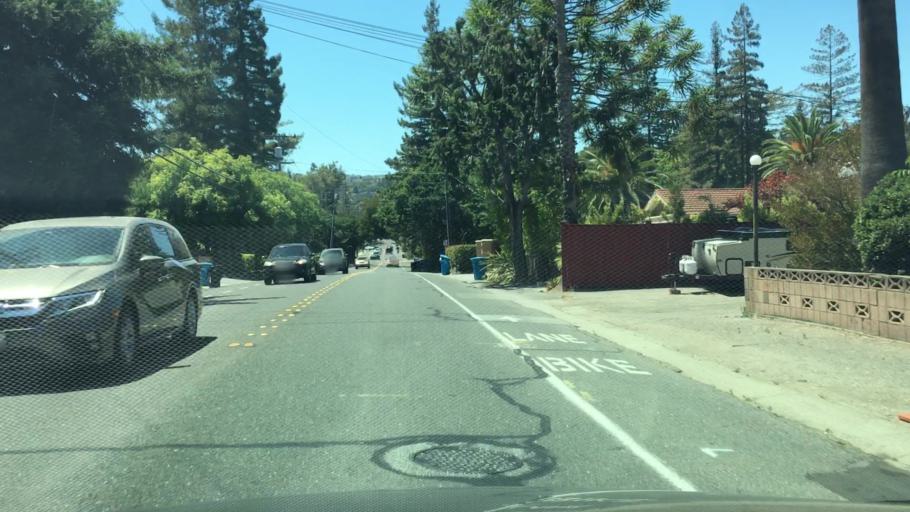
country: US
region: California
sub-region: San Mateo County
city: Emerald Lake Hills
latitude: 37.4810
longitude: -122.2580
